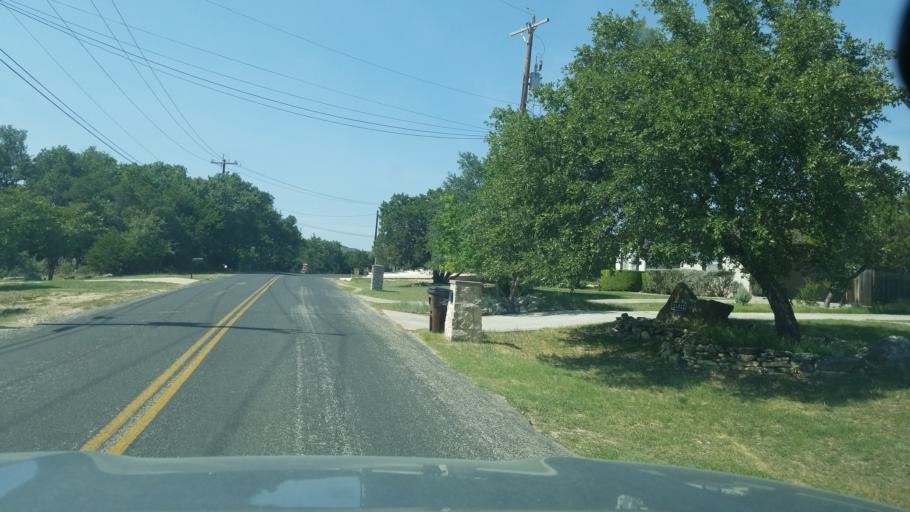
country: US
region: Texas
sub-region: Bexar County
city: Timberwood Park
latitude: 29.6920
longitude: -98.4902
